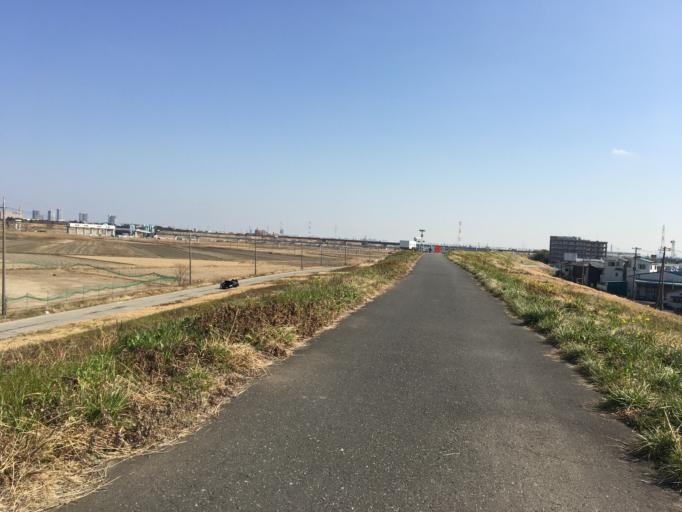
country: JP
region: Saitama
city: Shiki
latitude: 35.8404
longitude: 139.5955
